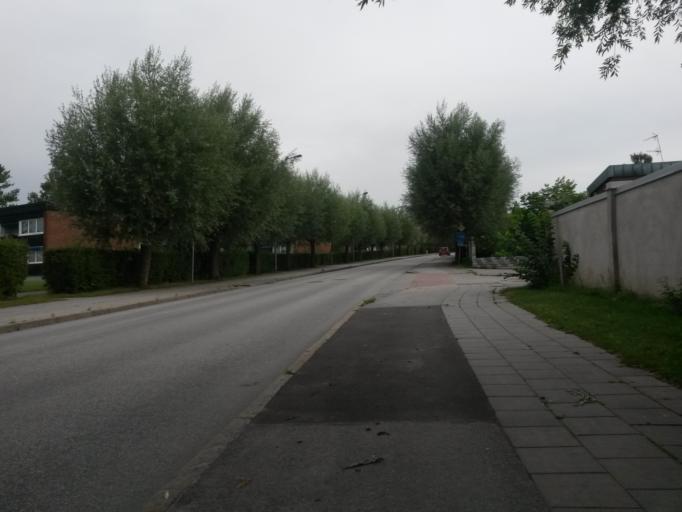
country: SE
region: Skane
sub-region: Lunds Kommun
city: Lund
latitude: 55.7033
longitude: 13.2302
